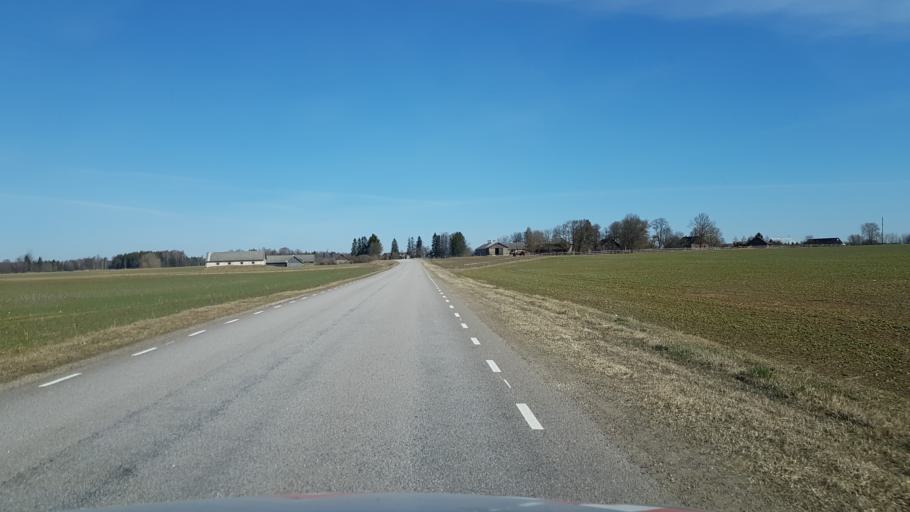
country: EE
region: Laeaene-Virumaa
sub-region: Vinni vald
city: Vinni
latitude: 59.2479
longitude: 26.3549
